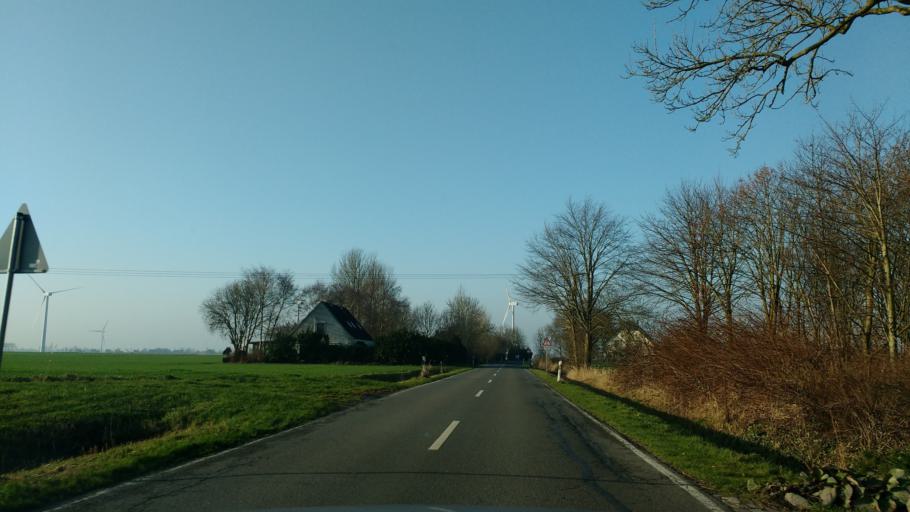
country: DE
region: Schleswig-Holstein
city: Trennewurth
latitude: 54.0007
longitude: 9.0190
